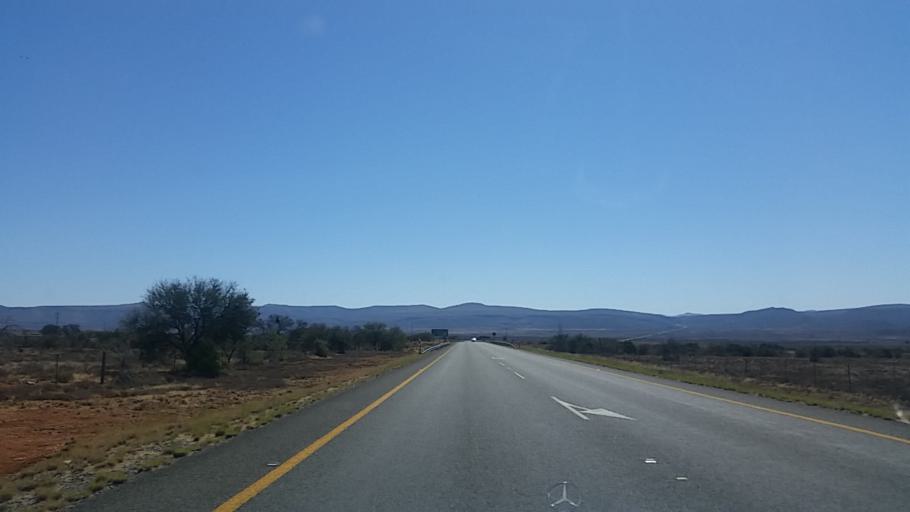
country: ZA
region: Eastern Cape
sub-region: Cacadu District Municipality
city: Graaff-Reinet
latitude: -32.0350
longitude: 24.6230
